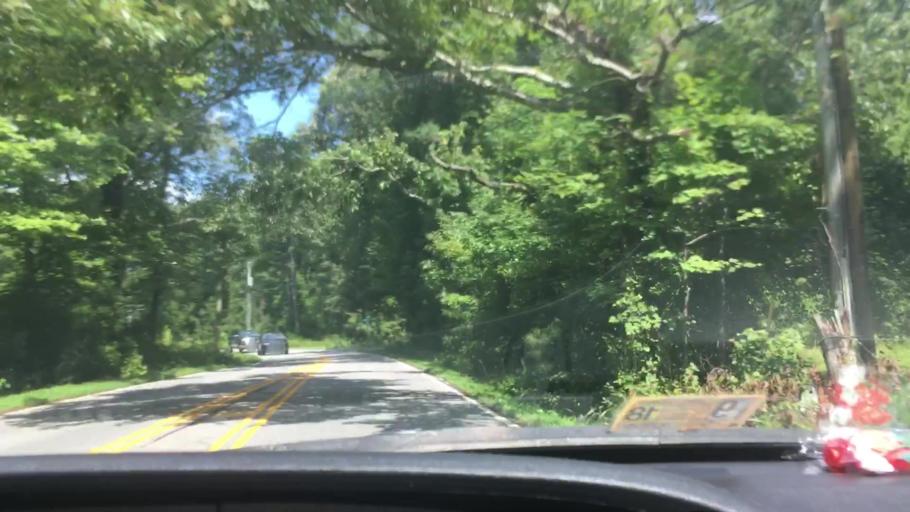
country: US
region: Virginia
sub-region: City of Virginia Beach
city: Virginia Beach
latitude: 36.7359
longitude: -76.1002
